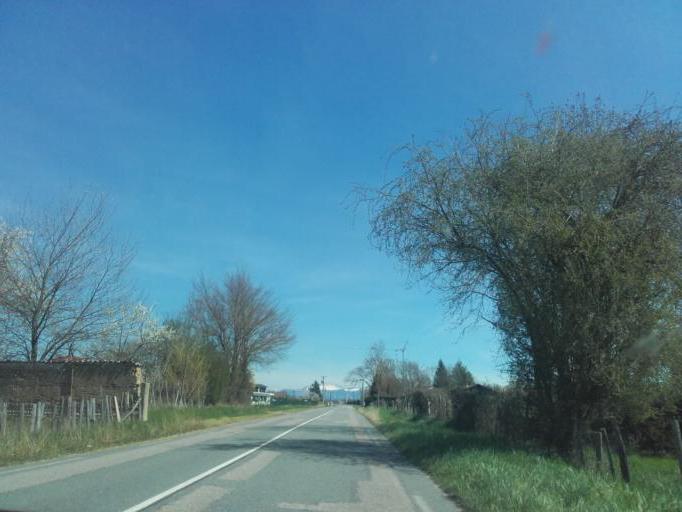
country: FR
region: Rhone-Alpes
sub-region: Departement de l'Isere
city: Brezins
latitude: 45.3368
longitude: 5.3089
